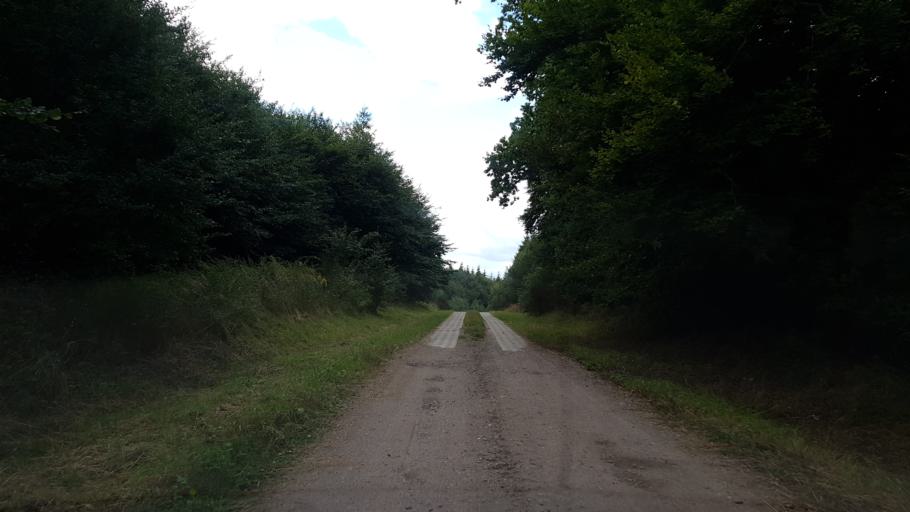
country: PL
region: West Pomeranian Voivodeship
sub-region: Powiat szczecinecki
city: Grzmiaca
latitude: 53.9609
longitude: 16.3982
